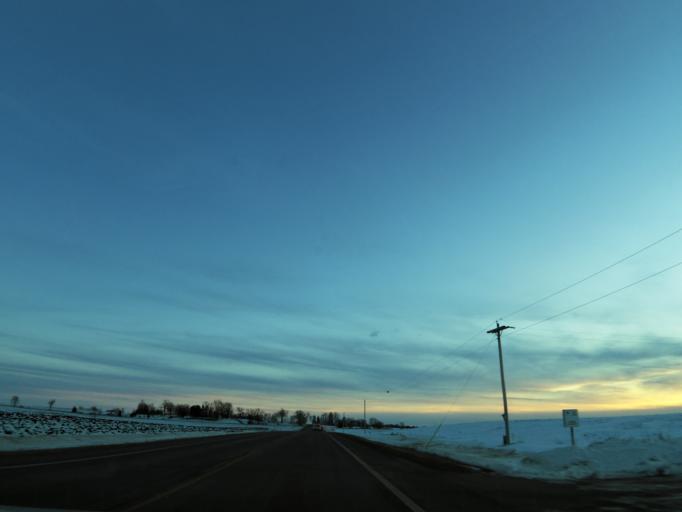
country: US
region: Minnesota
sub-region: Carver County
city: Chaska
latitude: 44.7369
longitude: -93.5622
